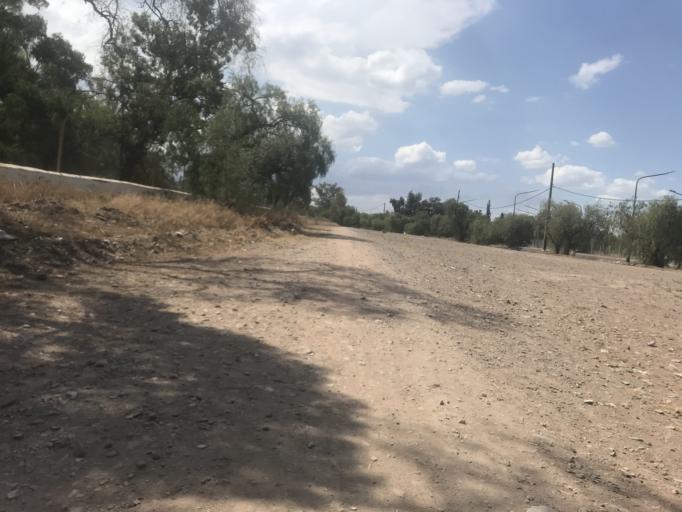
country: AR
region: Mendoza
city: Mendoza
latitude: -32.8863
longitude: -68.8849
